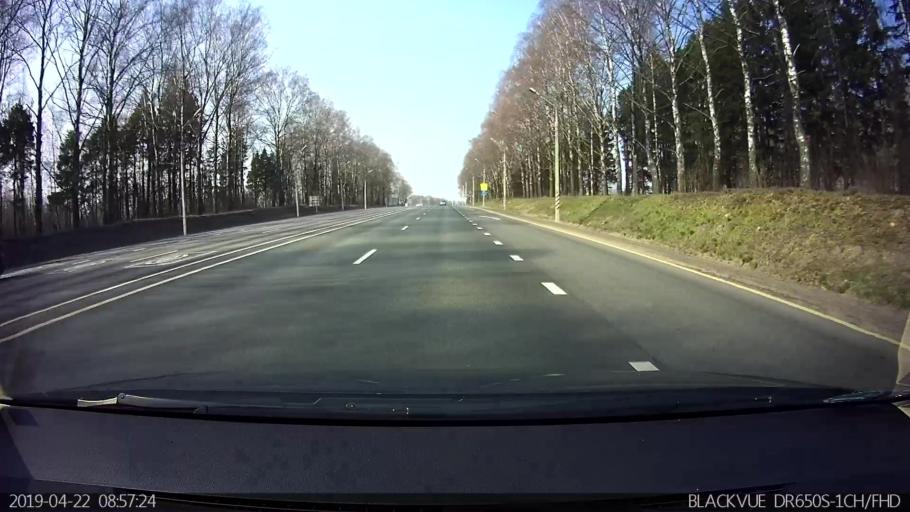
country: RU
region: Smolensk
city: Pechersk
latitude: 54.8692
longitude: 32.0175
